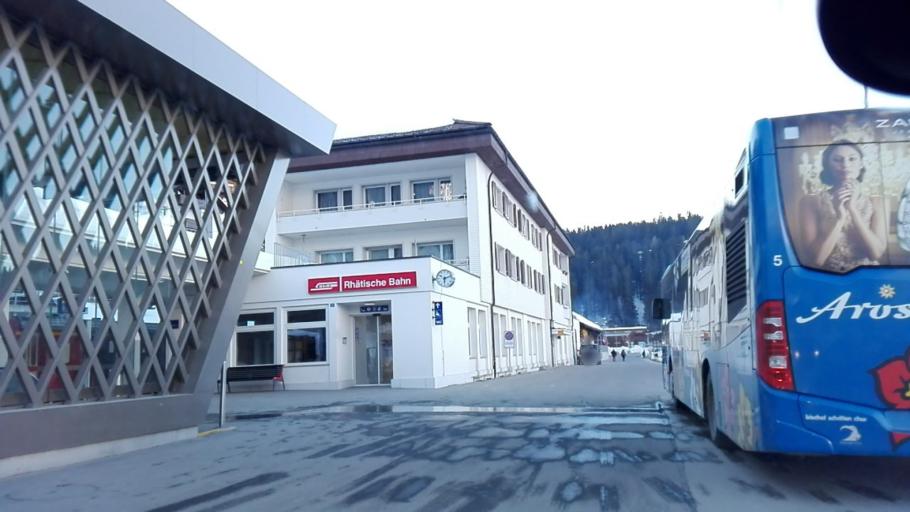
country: CH
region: Grisons
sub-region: Plessur District
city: Arosa
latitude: 46.7835
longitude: 9.6795
